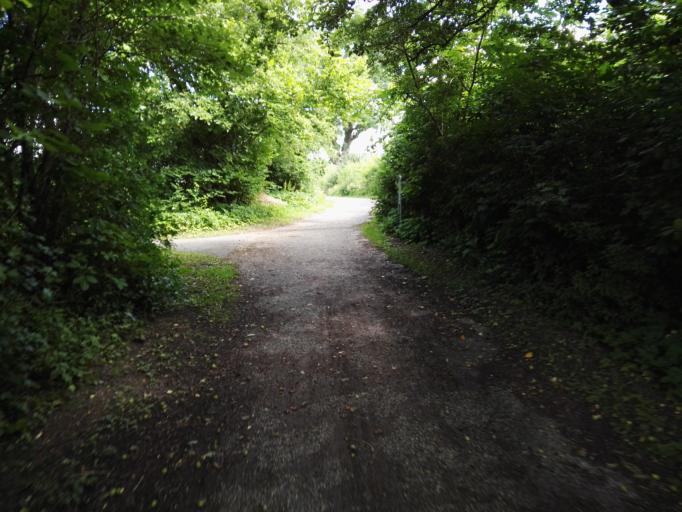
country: DK
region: Capital Region
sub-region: Herlev Kommune
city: Herlev
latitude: 55.7367
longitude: 12.4096
